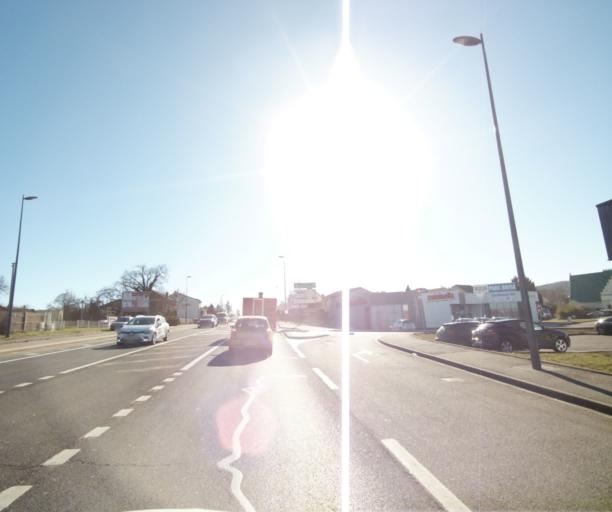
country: FR
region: Lorraine
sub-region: Departement de Meurthe-et-Moselle
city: Vandoeuvre-les-Nancy
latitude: 48.6540
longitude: 6.1856
